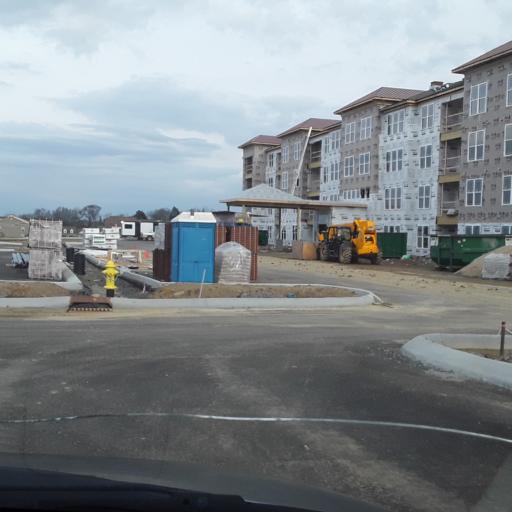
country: US
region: Tennessee
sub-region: Wilson County
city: Lebanon
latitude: 36.2313
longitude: -86.3700
